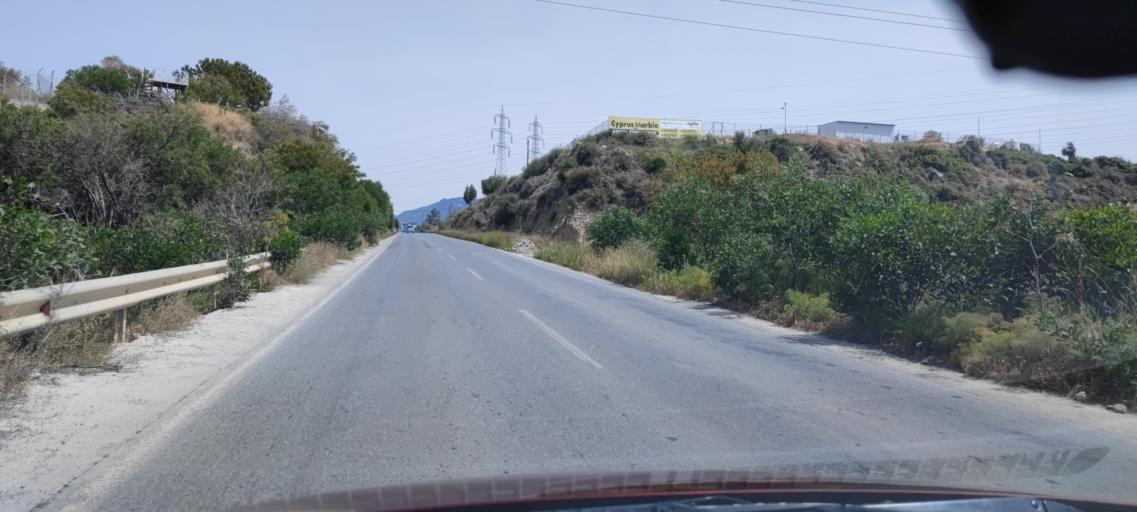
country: CY
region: Keryneia
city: Kyrenia
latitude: 35.3317
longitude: 33.4561
